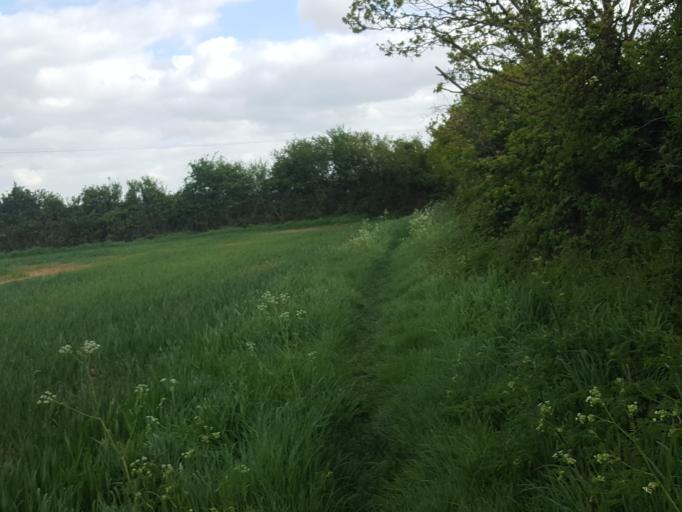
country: GB
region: England
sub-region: Essex
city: Frinton-on-Sea
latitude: 51.8374
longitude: 1.2073
